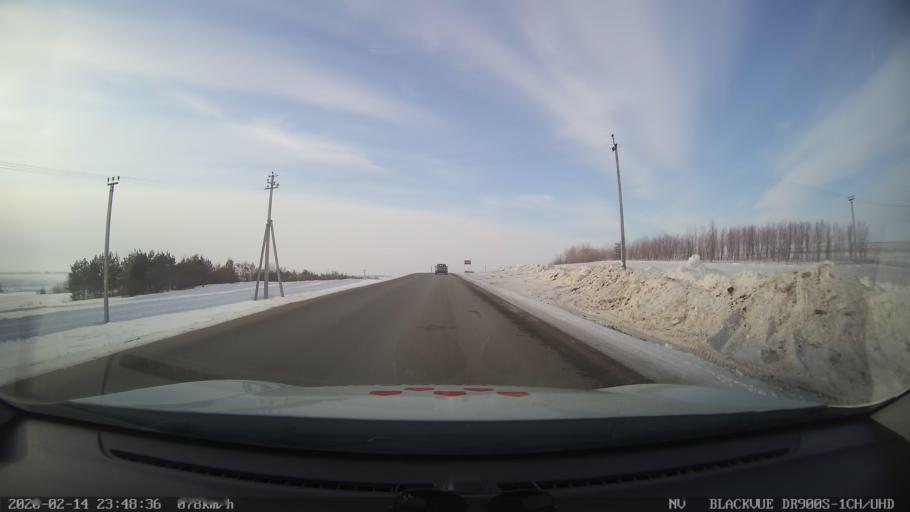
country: RU
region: Tatarstan
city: Kuybyshevskiy Zaton
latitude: 55.2487
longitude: 49.2000
